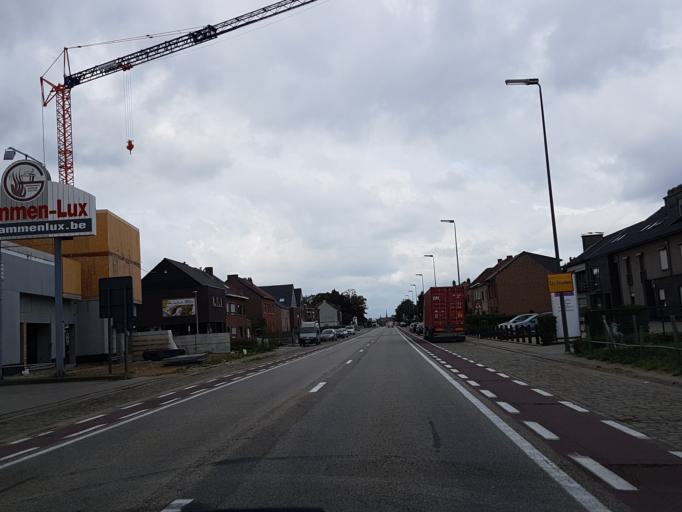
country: BE
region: Flanders
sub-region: Provincie Limburg
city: Sint-Truiden
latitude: 50.8047
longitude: 5.2012
